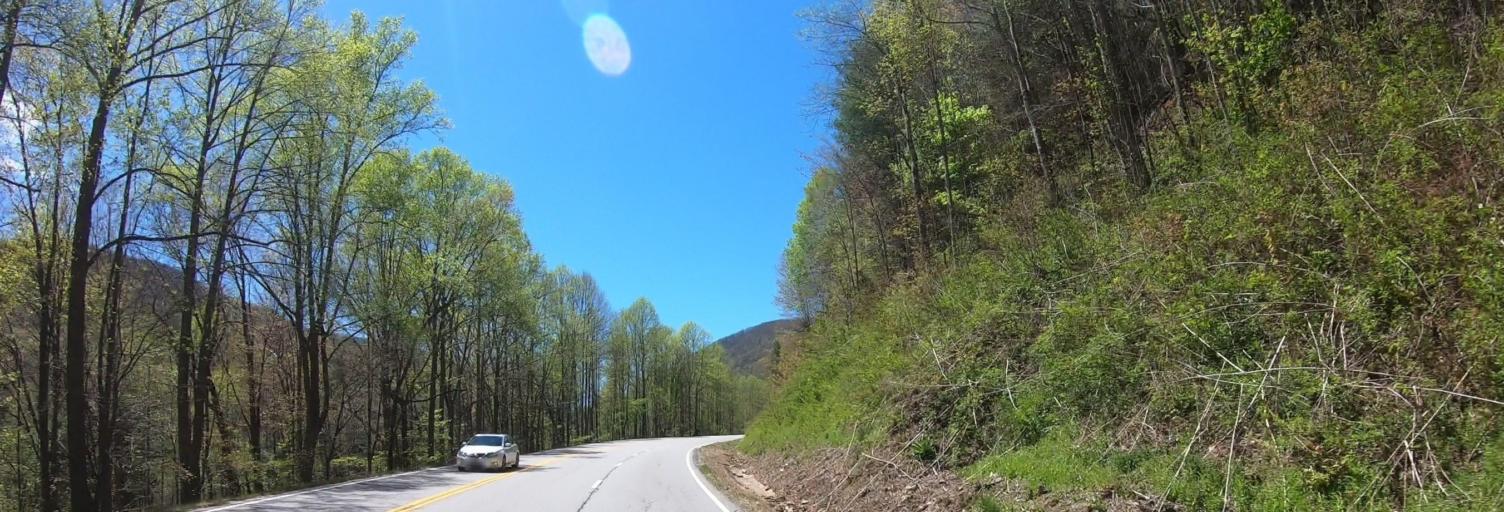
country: US
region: Georgia
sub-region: Towns County
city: Hiawassee
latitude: 34.8193
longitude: -83.7384
